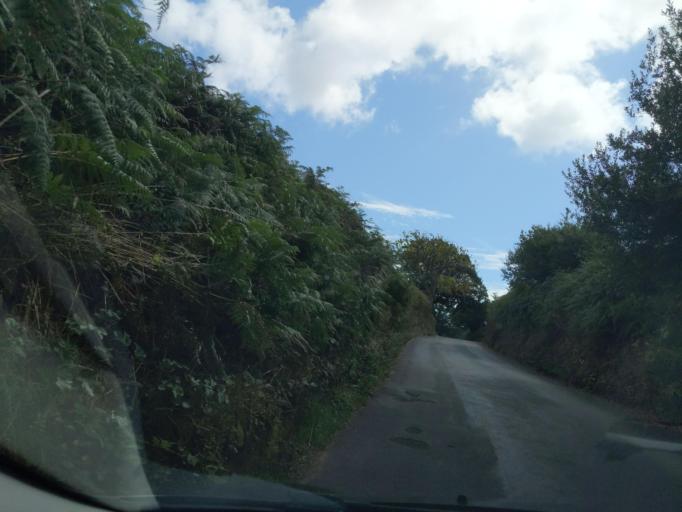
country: GB
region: England
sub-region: Devon
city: Modbury
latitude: 50.3610
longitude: -3.8958
